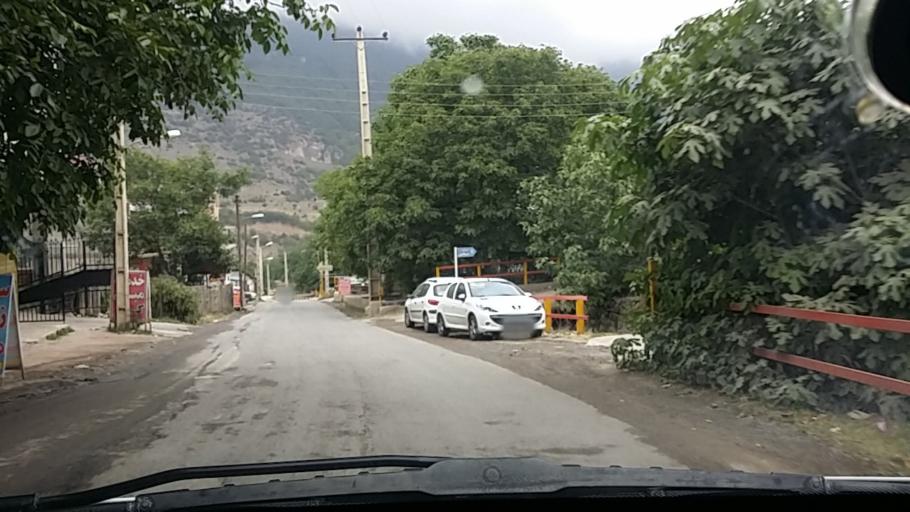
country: IR
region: Mazandaran
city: `Abbasabad
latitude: 36.4837
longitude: 51.1359
